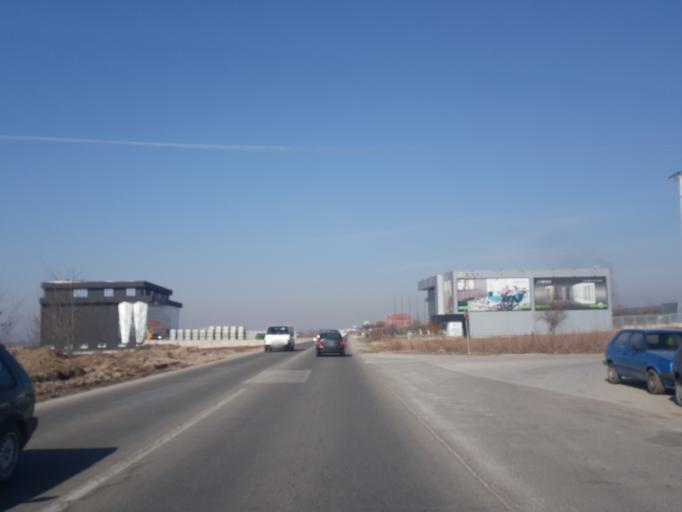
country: XK
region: Mitrovica
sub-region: Vushtrri
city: Vushtrri
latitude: 42.7679
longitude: 21.0234
